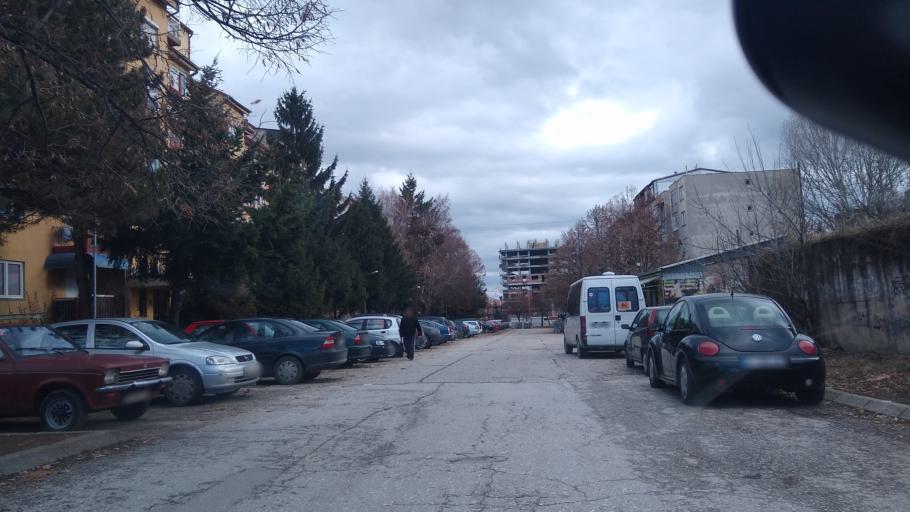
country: MK
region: Bitola
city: Bitola
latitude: 41.0287
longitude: 21.3120
